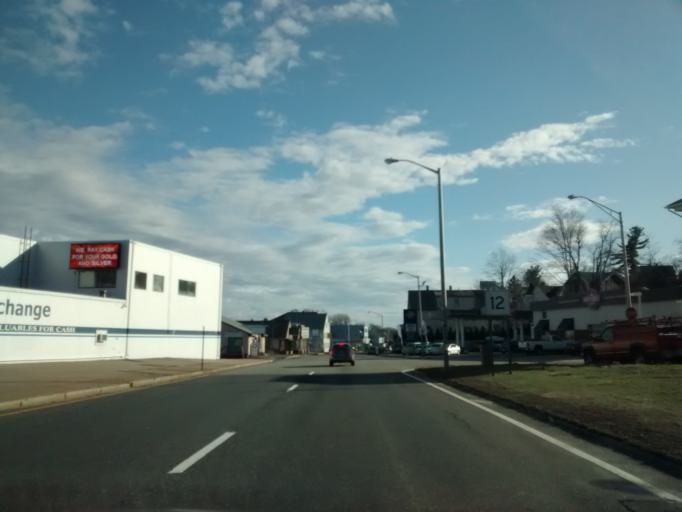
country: US
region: Massachusetts
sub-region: Worcester County
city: Worcester
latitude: 42.2944
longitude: -71.8041
